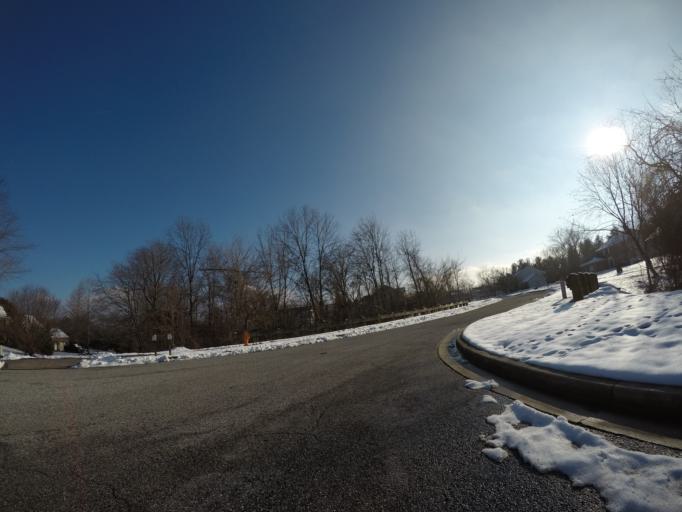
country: US
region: Maryland
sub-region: Howard County
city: Ilchester
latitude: 39.2196
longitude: -76.7861
